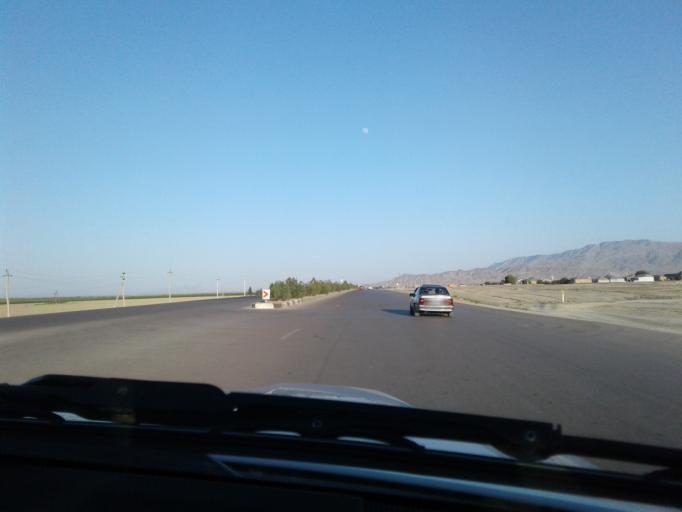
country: TM
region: Ahal
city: Baharly
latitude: 38.3168
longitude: 57.6025
